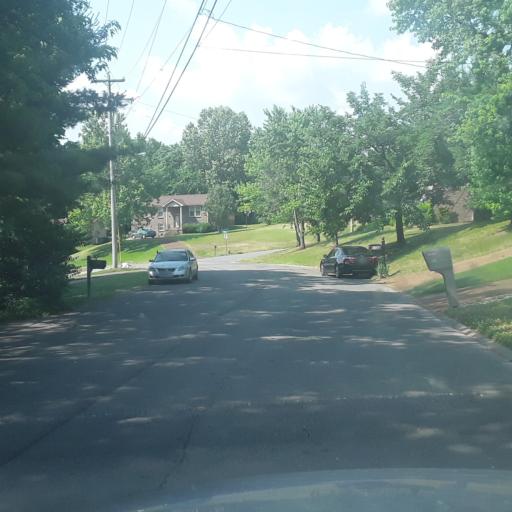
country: US
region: Tennessee
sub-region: Williamson County
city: Brentwood Estates
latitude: 36.0358
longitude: -86.7077
